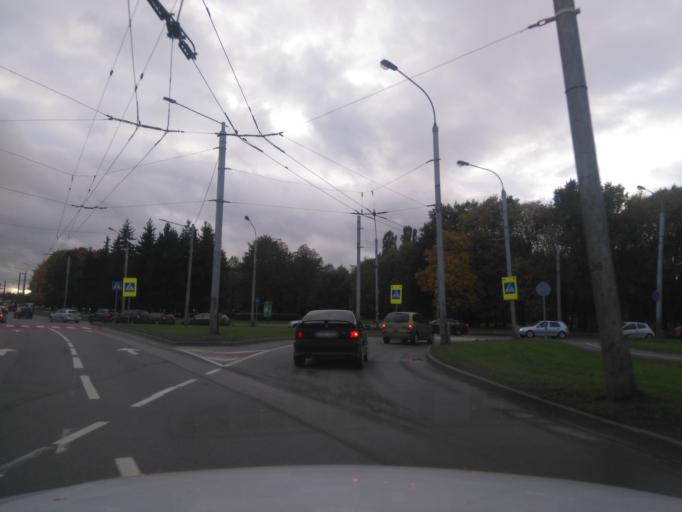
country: LT
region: Kauno apskritis
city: Dainava (Kaunas)
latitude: 54.9134
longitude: 23.9746
